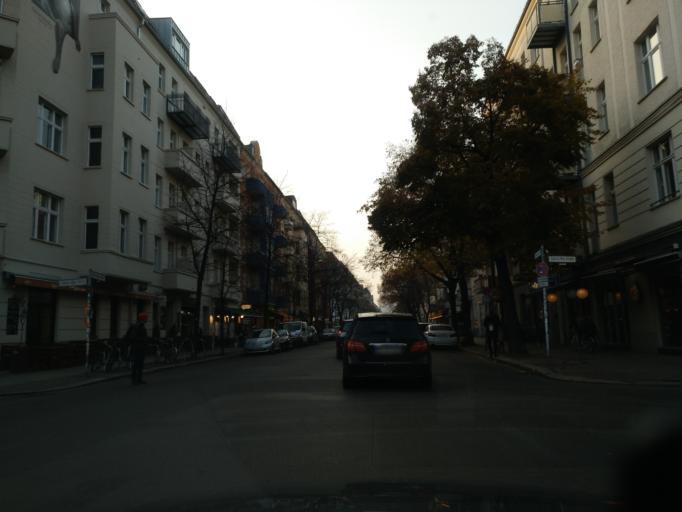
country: DE
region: Berlin
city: Friedrichshain Bezirk
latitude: 52.5115
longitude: 13.4589
